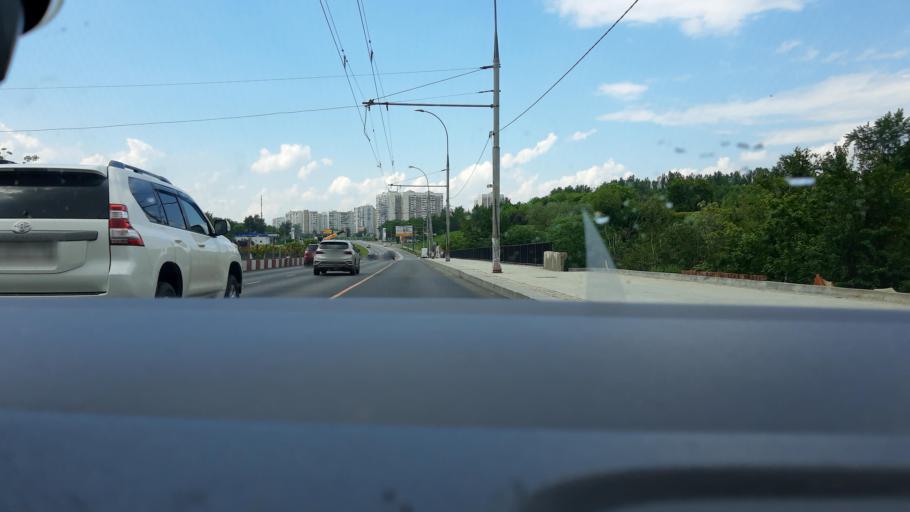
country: RU
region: Moskovskaya
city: Kur'yanovo
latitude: 55.6308
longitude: 37.7066
